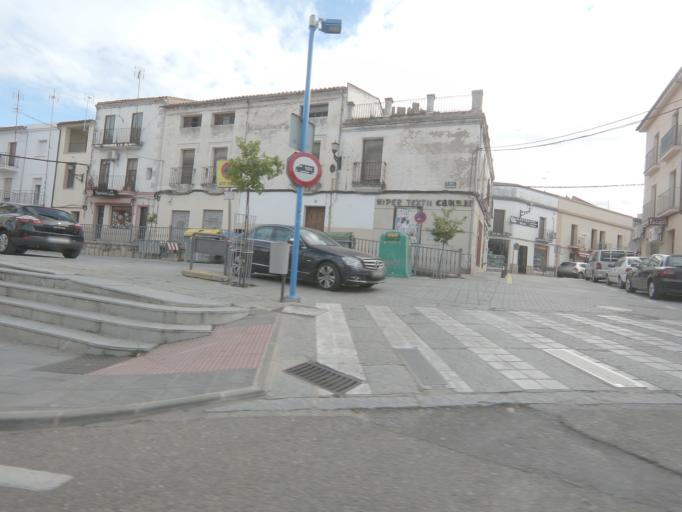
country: ES
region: Extremadura
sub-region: Provincia de Caceres
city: Coria
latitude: 39.9850
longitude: -6.5361
